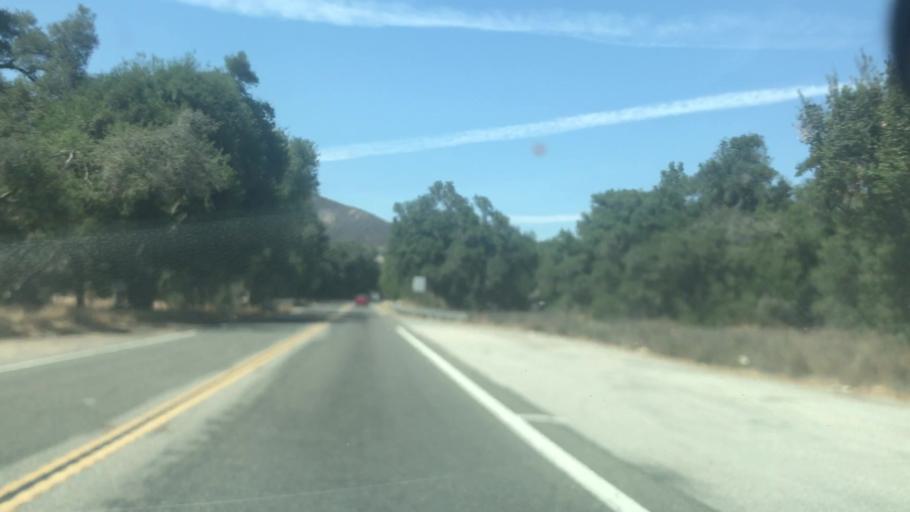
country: US
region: California
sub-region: Riverside County
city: Lakeland Village
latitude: 33.6385
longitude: -117.4219
